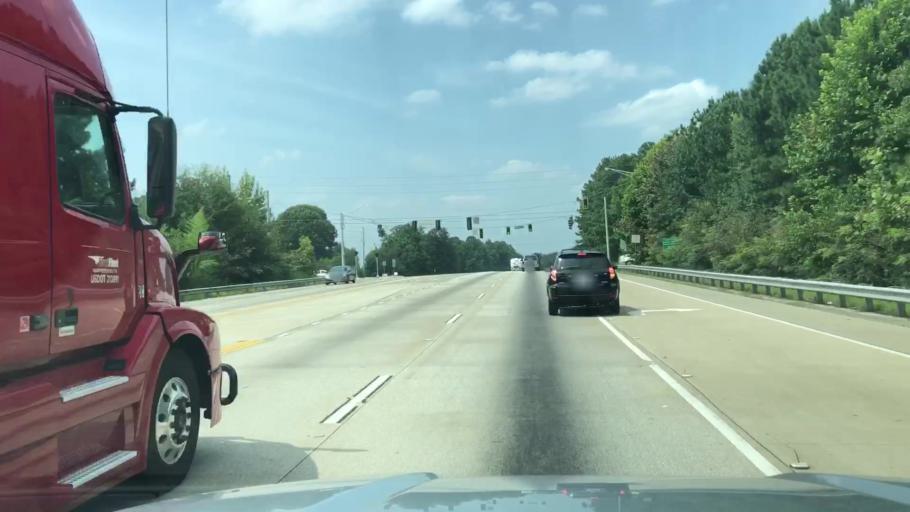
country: US
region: Georgia
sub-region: Douglas County
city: Lithia Springs
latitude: 33.8071
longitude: -84.6535
